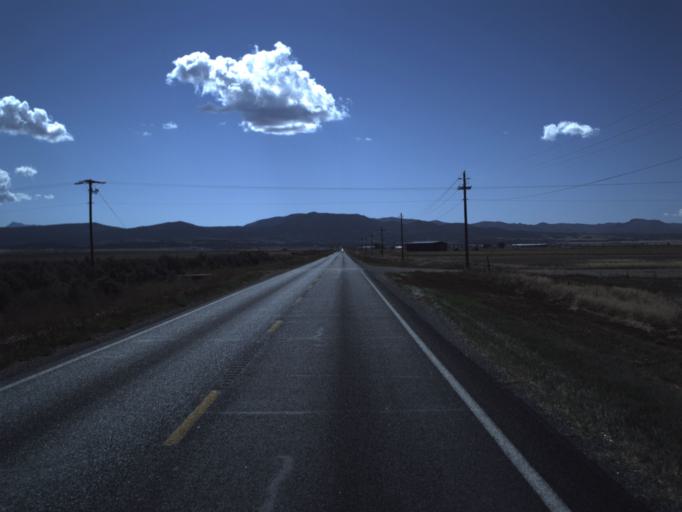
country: US
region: Utah
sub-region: Washington County
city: Enterprise
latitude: 37.6348
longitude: -113.6612
